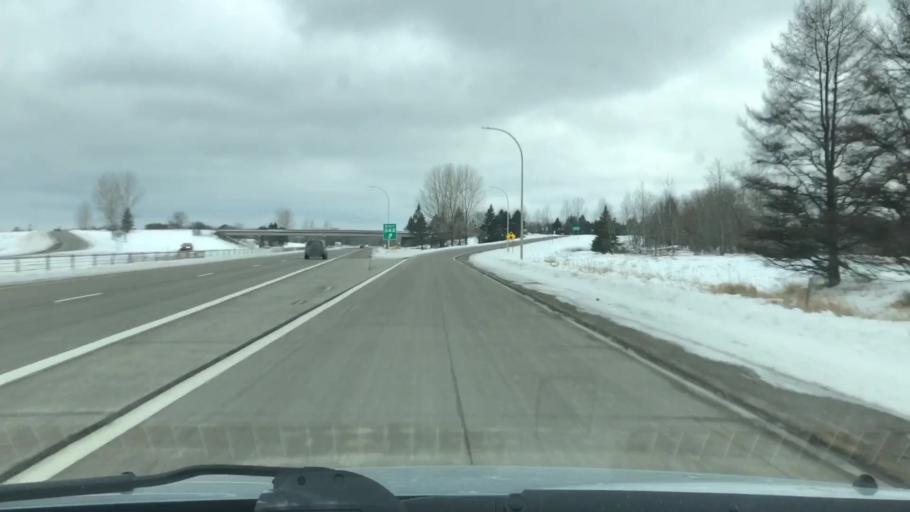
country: US
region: Minnesota
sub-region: Carlton County
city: Esko
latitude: 46.6966
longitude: -92.3606
